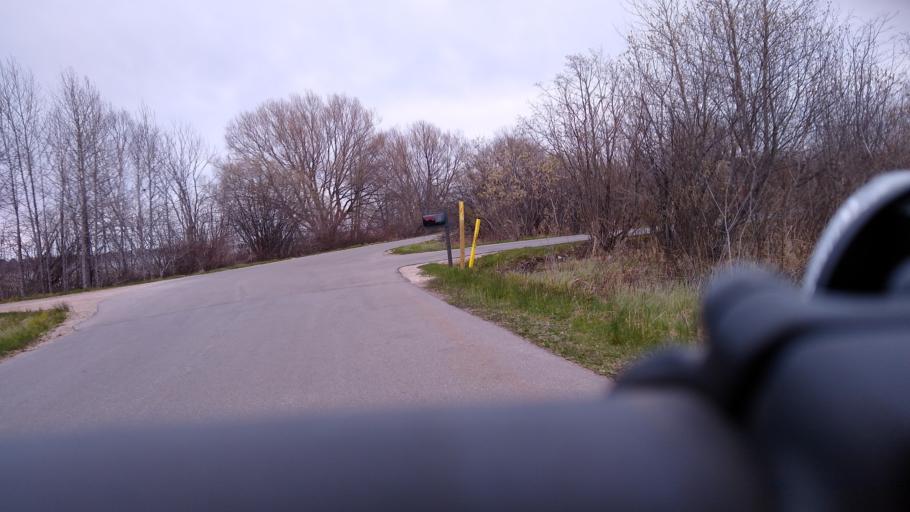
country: US
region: Michigan
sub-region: Delta County
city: Escanaba
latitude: 45.7060
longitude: -87.0812
